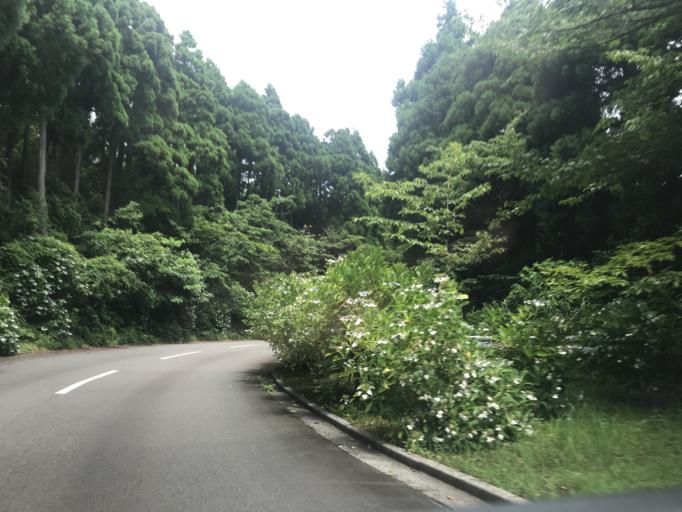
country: JP
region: Shizuoka
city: Ito
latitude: 34.7637
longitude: 139.4230
